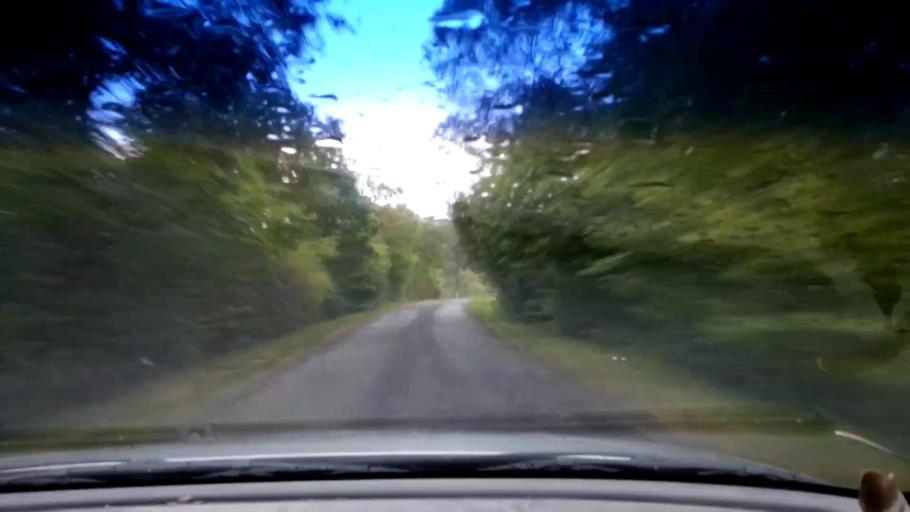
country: DE
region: Bavaria
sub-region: Upper Franconia
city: Priesendorf
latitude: 49.8750
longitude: 10.6682
